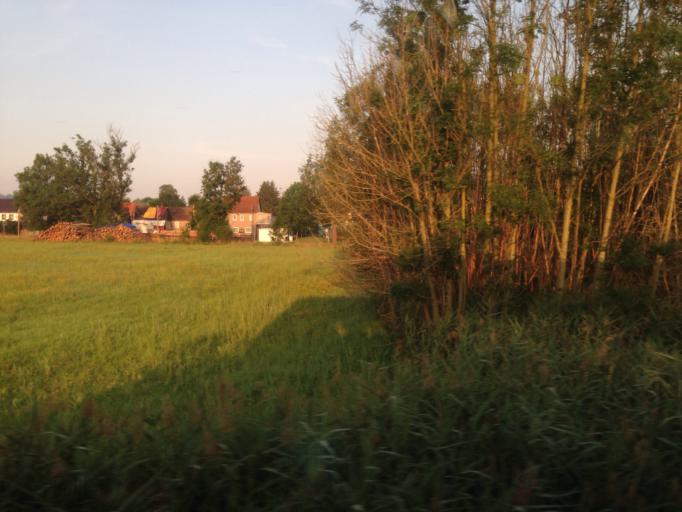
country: DE
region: Thuringia
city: Bodelwitz
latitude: 50.7063
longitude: 11.6141
